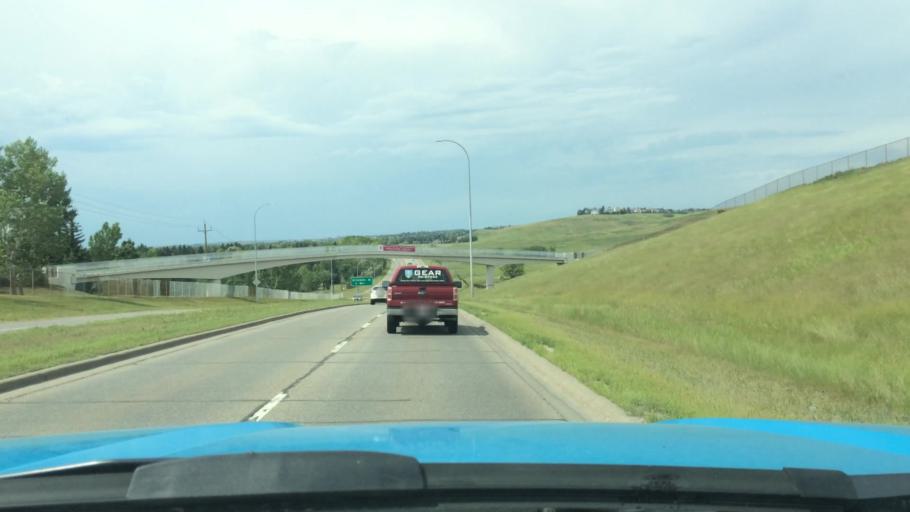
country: CA
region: Alberta
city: Calgary
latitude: 51.1009
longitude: -114.1231
